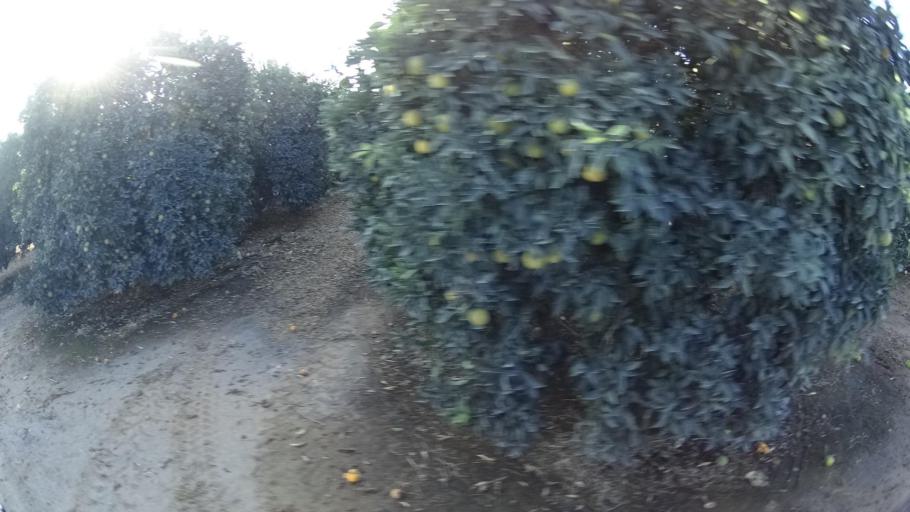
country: US
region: California
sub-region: Tulare County
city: Richgrove
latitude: 35.7763
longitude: -119.0934
